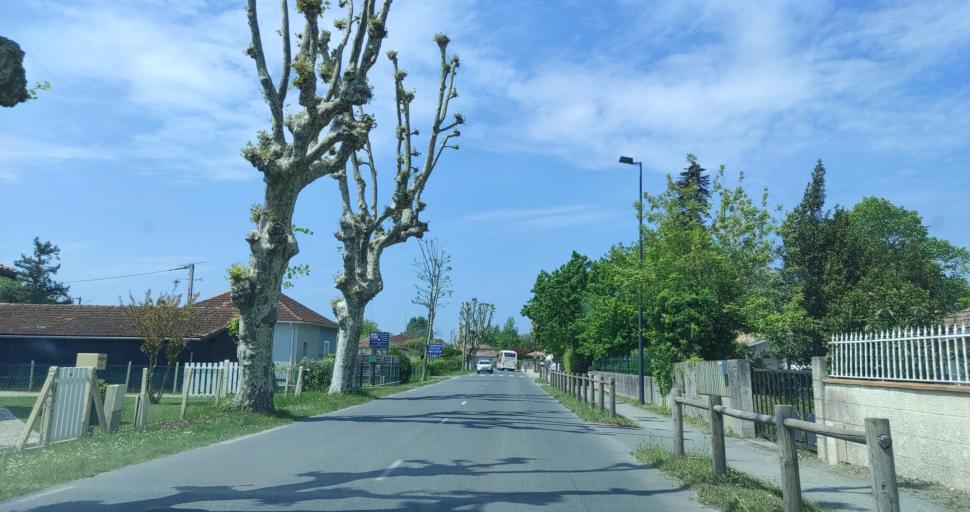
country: FR
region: Aquitaine
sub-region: Departement de la Gironde
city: Ares
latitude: 44.7640
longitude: -1.1345
